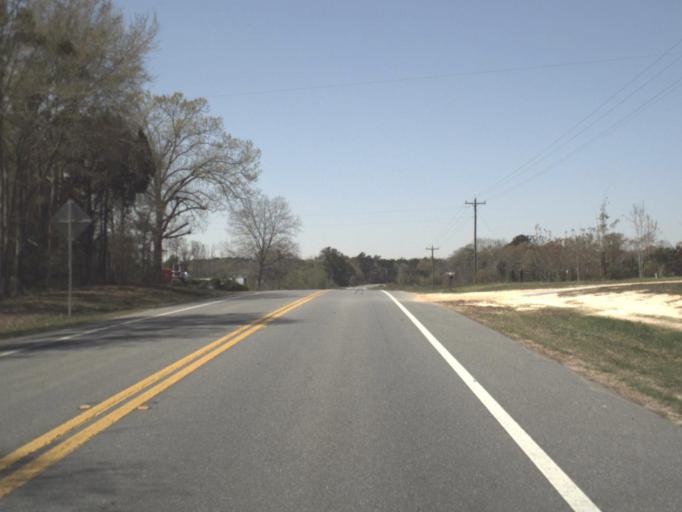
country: US
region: Alabama
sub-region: Geneva County
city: Hartford
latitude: 30.9594
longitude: -85.6690
